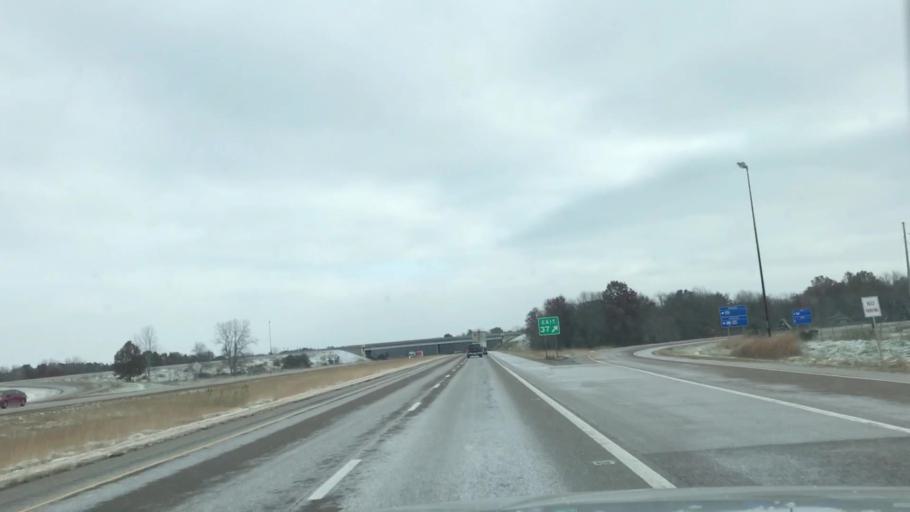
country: US
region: Illinois
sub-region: Macoupin County
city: Staunton
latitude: 38.9650
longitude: -89.7567
